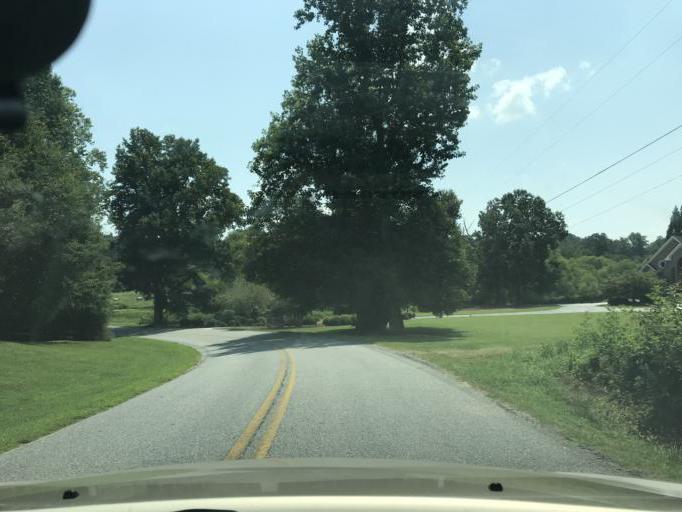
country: US
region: Georgia
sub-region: Dawson County
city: Dawsonville
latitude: 34.3221
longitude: -84.0941
